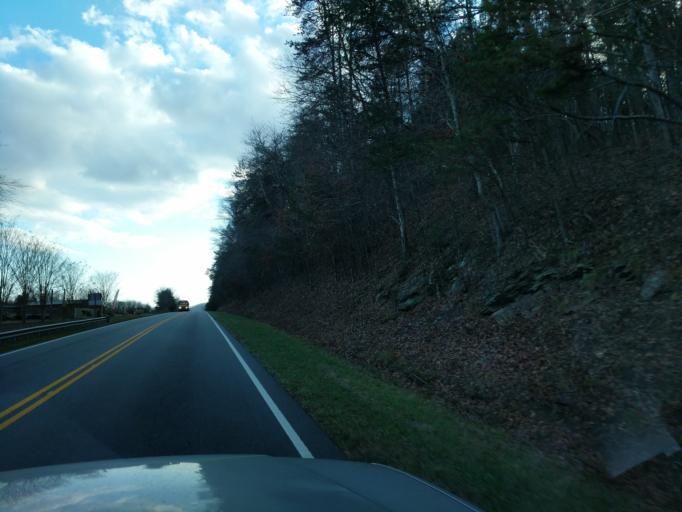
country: US
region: North Carolina
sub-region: McDowell County
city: West Marion
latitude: 35.6060
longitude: -81.9848
